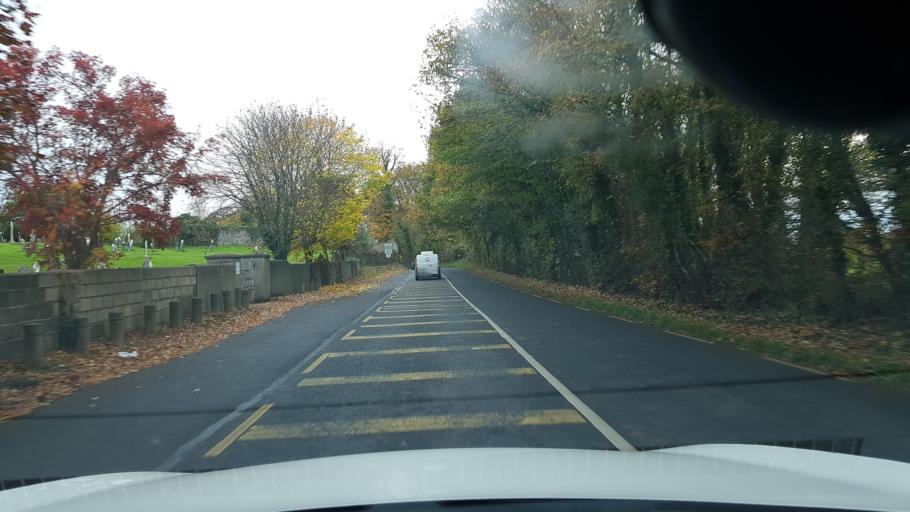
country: IE
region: Leinster
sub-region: Fingal County
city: Blanchardstown
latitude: 53.4113
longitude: -6.3892
